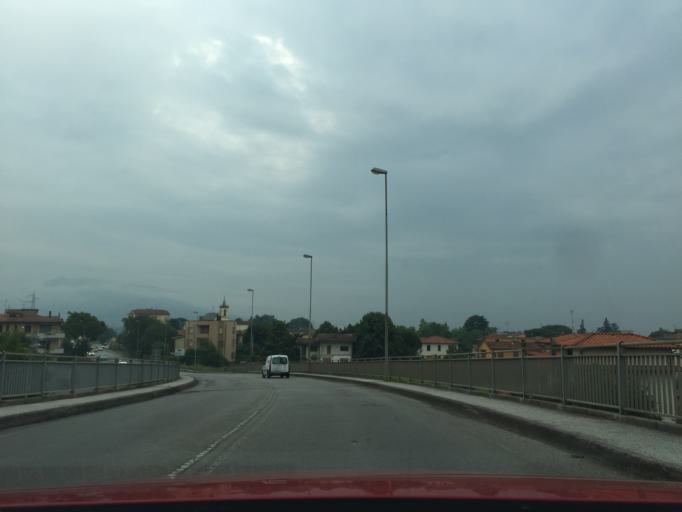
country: IT
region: Tuscany
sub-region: Provincia di Pistoia
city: Pistoia
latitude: 43.9443
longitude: 10.9029
